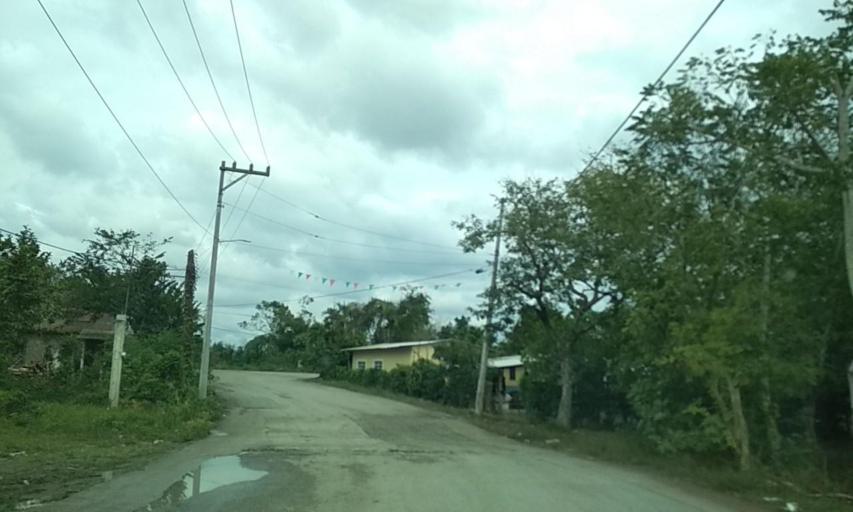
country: MX
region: Veracruz
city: Agua Dulce
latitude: 20.3586
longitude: -97.3360
